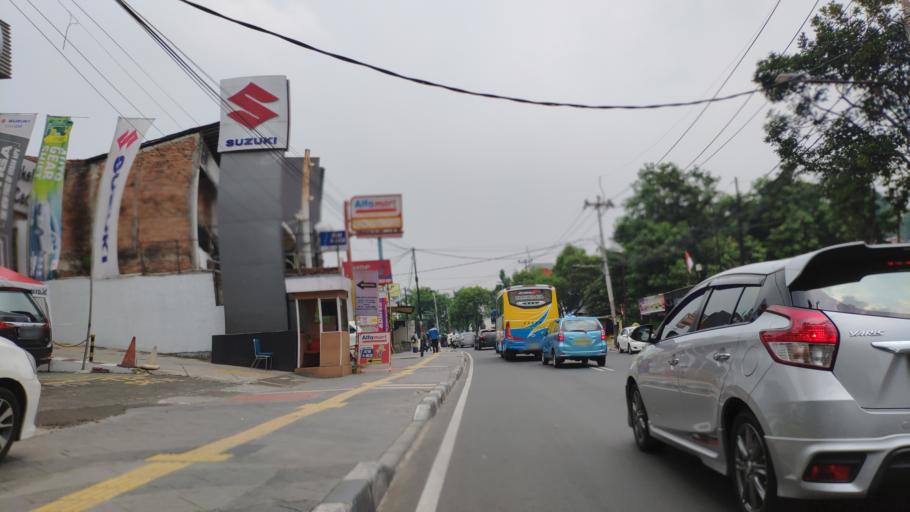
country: ID
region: Banten
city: South Tangerang
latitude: -6.2606
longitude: 106.7675
